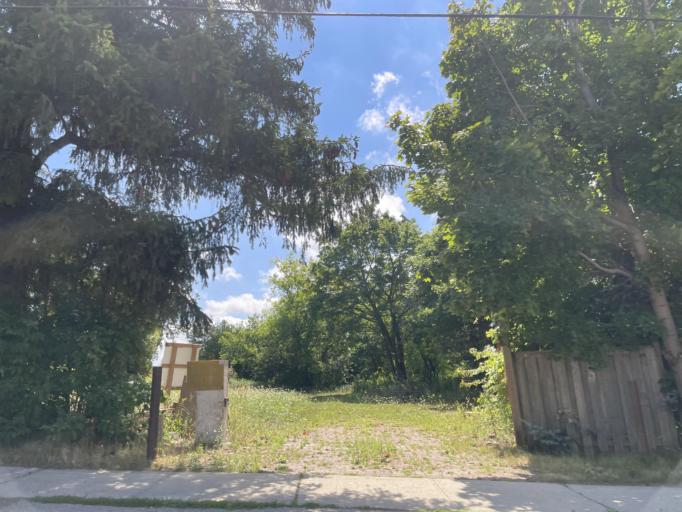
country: CA
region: Ontario
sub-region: Wellington County
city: Guelph
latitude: 43.5144
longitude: -80.1985
